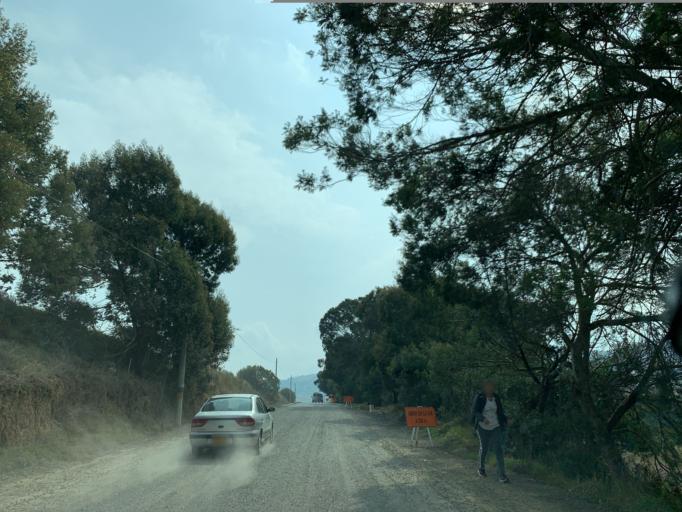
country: CO
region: Boyaca
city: Tunja
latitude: 5.5297
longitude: -73.3128
